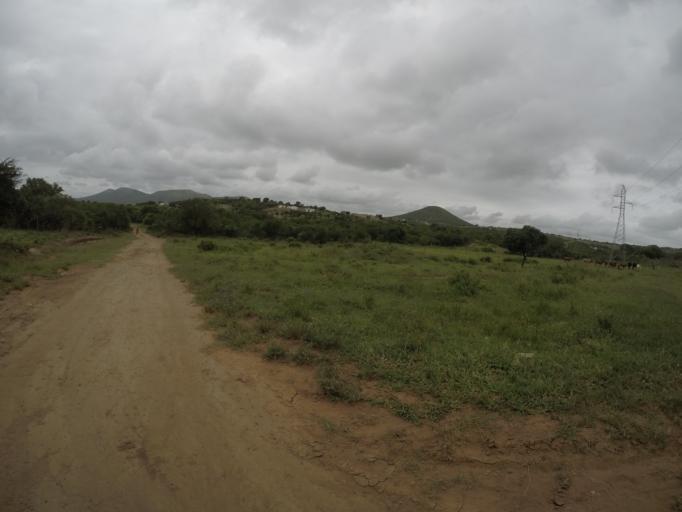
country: ZA
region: KwaZulu-Natal
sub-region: uThungulu District Municipality
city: Empangeni
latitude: -28.5925
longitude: 31.8409
